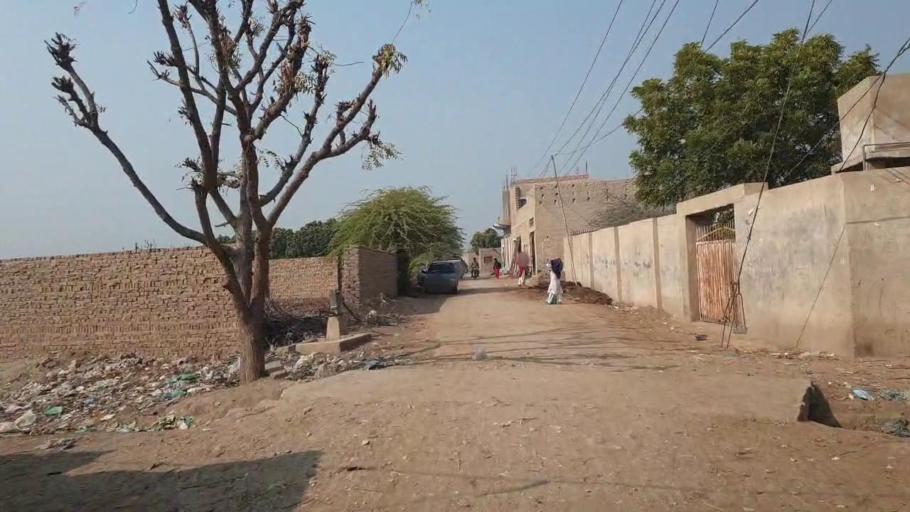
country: PK
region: Sindh
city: Hala
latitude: 25.8321
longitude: 68.4437
